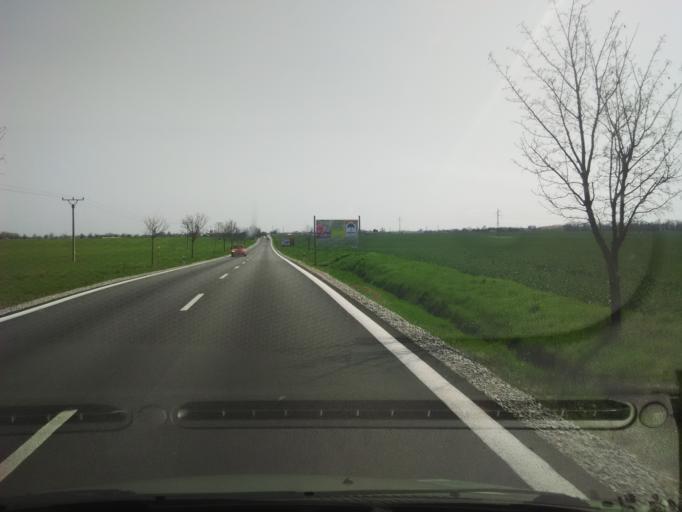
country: SK
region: Nitriansky
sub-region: Okres Nove Zamky
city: Nove Zamky
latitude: 48.0256
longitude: 18.1388
